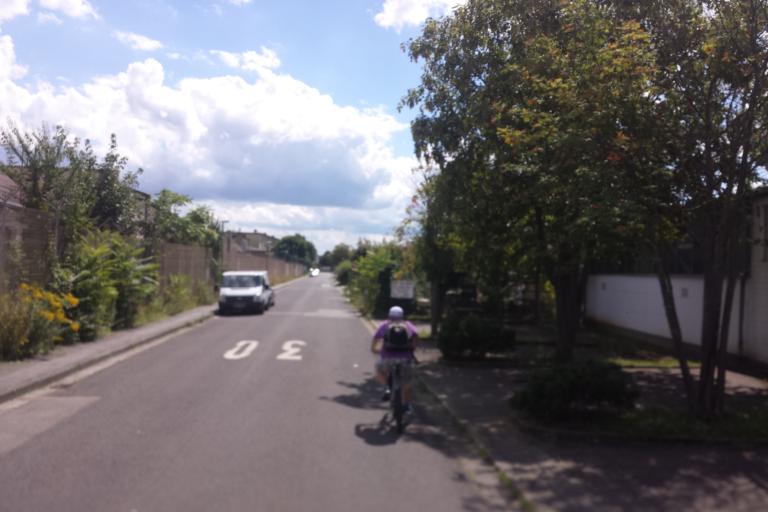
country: DE
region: Baden-Wuerttemberg
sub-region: Karlsruhe Region
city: Heidelberg
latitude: 49.3870
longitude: 8.6806
